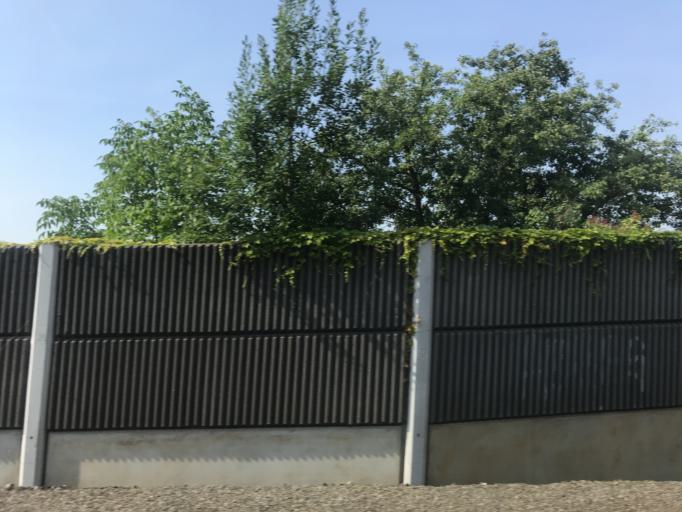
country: CZ
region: Central Bohemia
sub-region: Okres Praha-Vychod
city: Ricany
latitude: 50.0011
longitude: 14.6558
